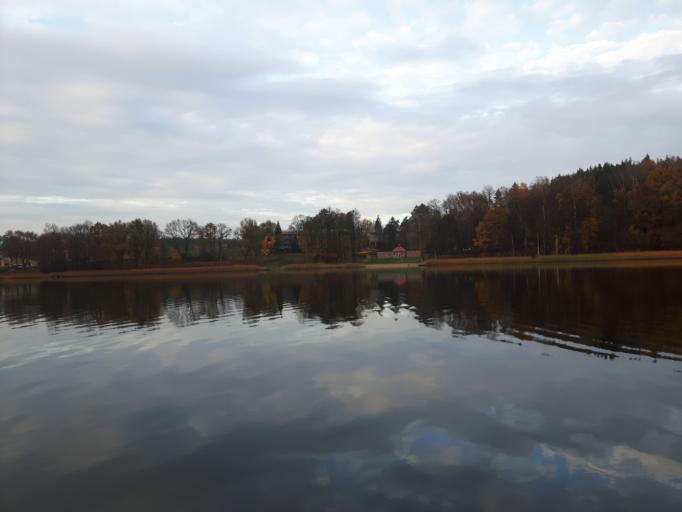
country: PL
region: Warmian-Masurian Voivodeship
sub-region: Powiat olsztynski
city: Barczewo
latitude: 53.8270
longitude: 20.7373
